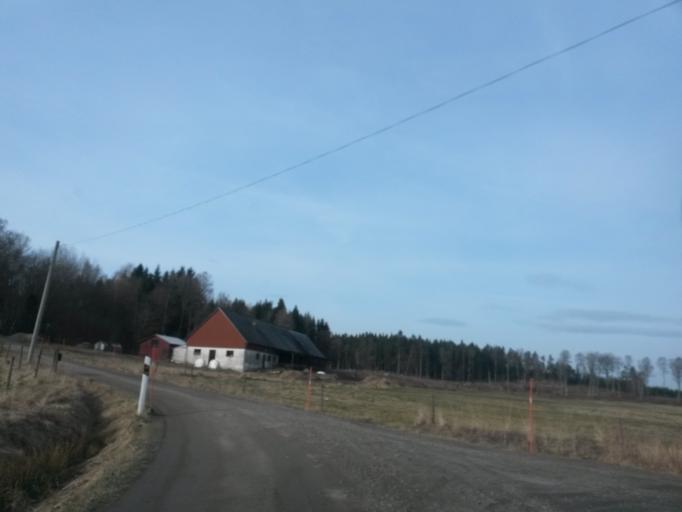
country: SE
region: Vaestra Goetaland
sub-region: Vargarda Kommun
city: Jonstorp
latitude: 58.0174
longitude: 12.7414
